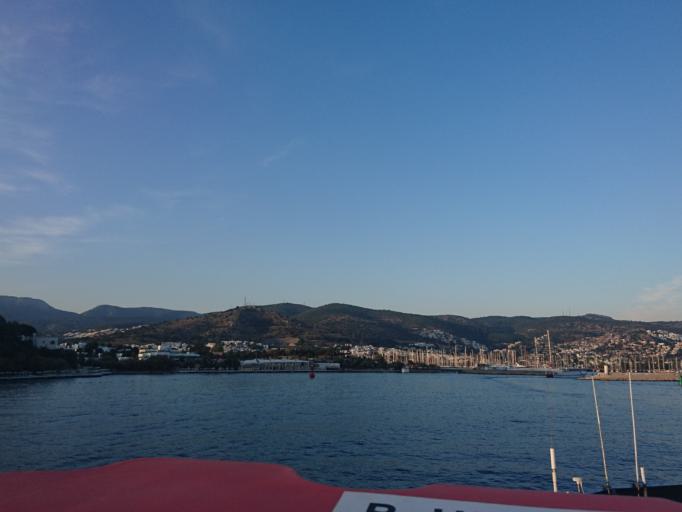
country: TR
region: Mugla
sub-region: Bodrum
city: Bodrum
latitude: 37.0281
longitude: 27.4225
